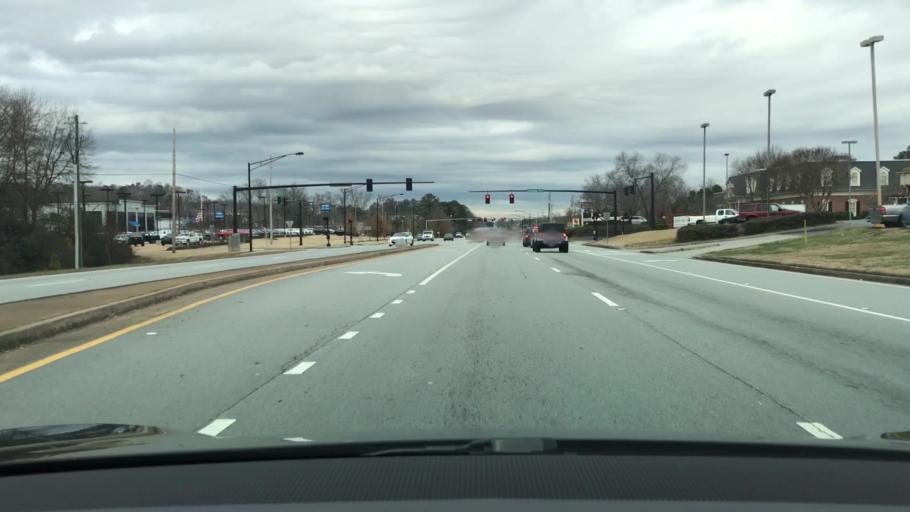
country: US
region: Georgia
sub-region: Gwinnett County
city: Buford
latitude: 34.1039
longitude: -84.0052
